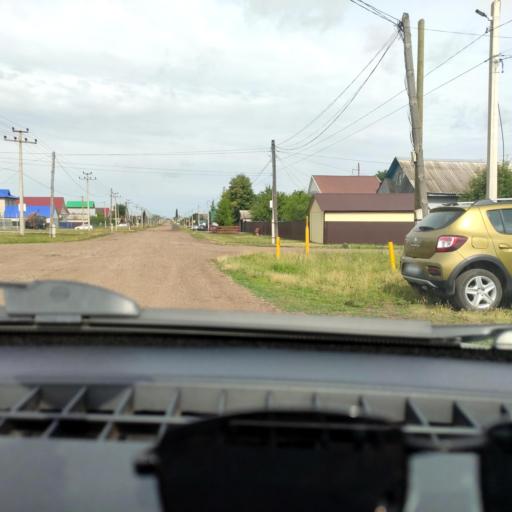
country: RU
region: Bashkortostan
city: Ulukulevo
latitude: 54.4216
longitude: 56.3349
